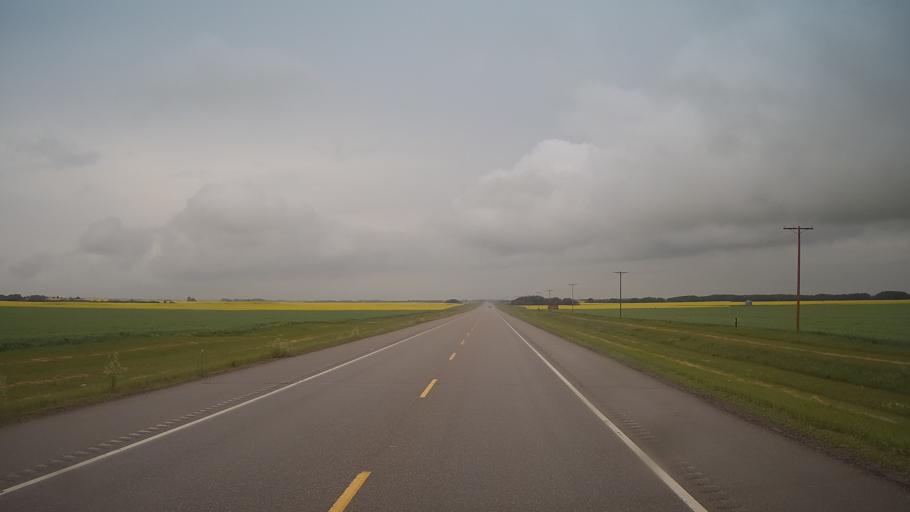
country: CA
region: Saskatchewan
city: Wilkie
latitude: 52.4225
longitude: -108.9003
